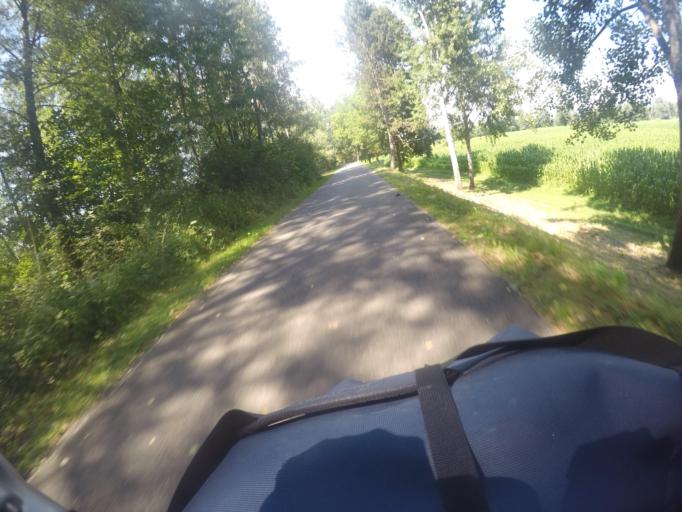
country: CH
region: Saint Gallen
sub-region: Wahlkreis Rheintal
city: Diepoldsau
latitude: 47.3890
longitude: 9.6764
